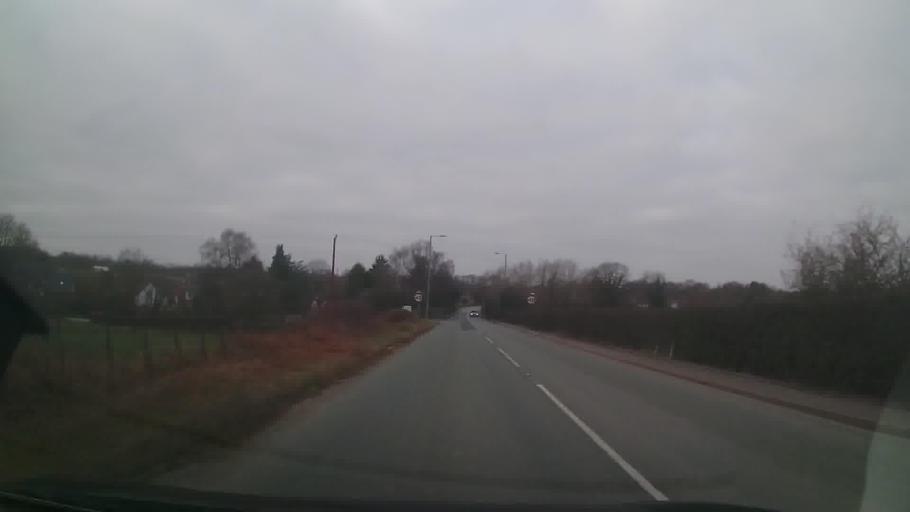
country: GB
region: England
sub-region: Shropshire
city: Ford
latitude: 52.7292
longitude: -2.8362
